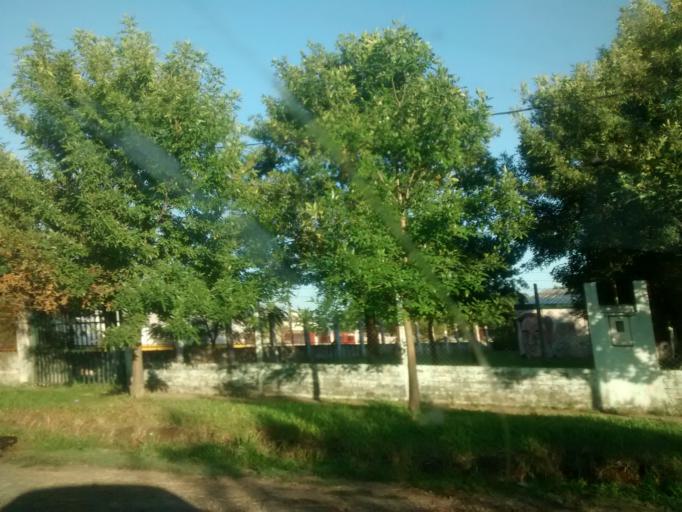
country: AR
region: Chaco
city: Resistencia
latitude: -27.4714
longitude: -58.9823
